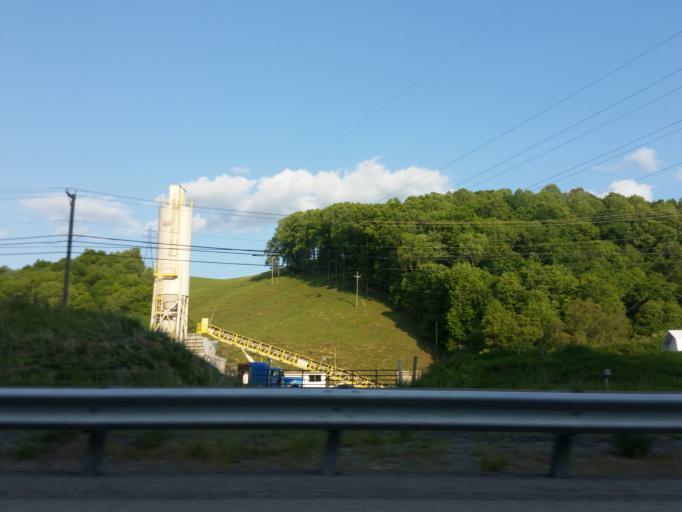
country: US
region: Virginia
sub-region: Russell County
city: Lebanon
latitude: 36.9168
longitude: -82.0065
